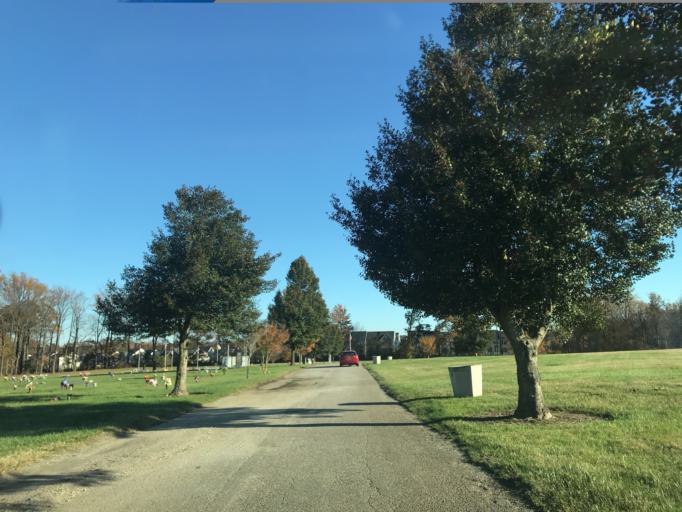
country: US
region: Maryland
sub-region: Baltimore County
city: White Marsh
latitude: 39.3588
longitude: -76.4198
